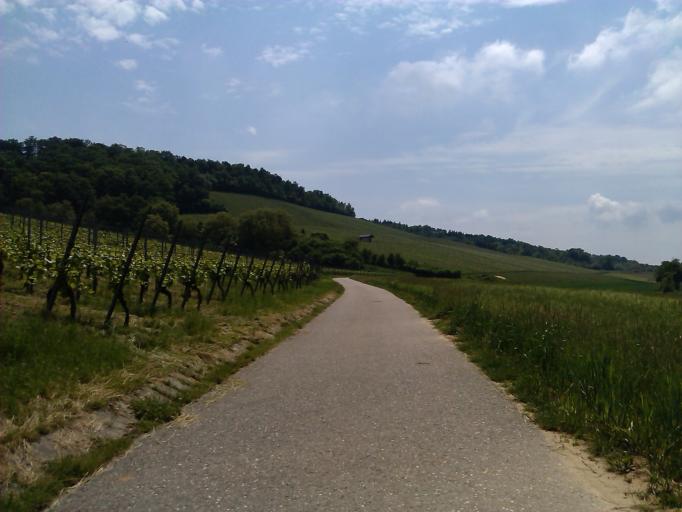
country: DE
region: Baden-Wuerttemberg
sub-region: Regierungsbezirk Stuttgart
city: Pfaffenhofen
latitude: 49.0984
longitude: 8.9836
